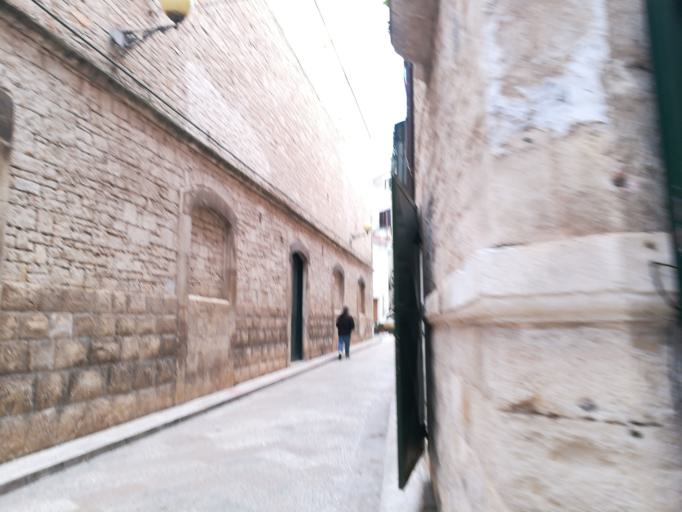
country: IT
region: Apulia
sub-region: Provincia di Bari
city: Bitonto
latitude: 41.1068
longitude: 16.6884
